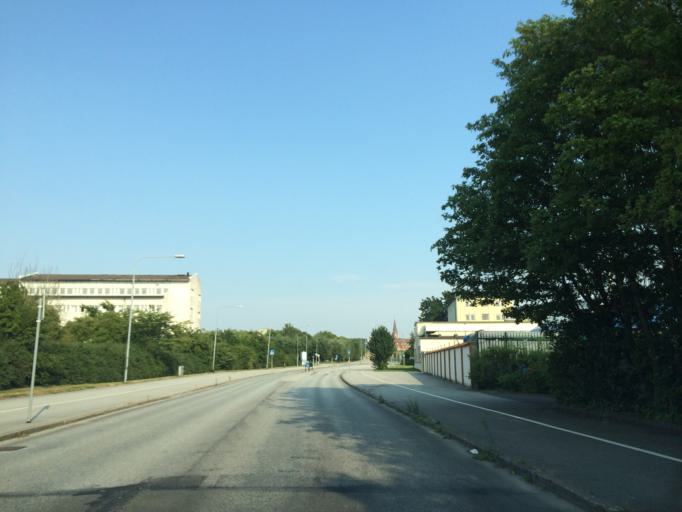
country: SE
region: Skane
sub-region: Lunds Kommun
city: Lund
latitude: 55.7134
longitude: 13.1773
